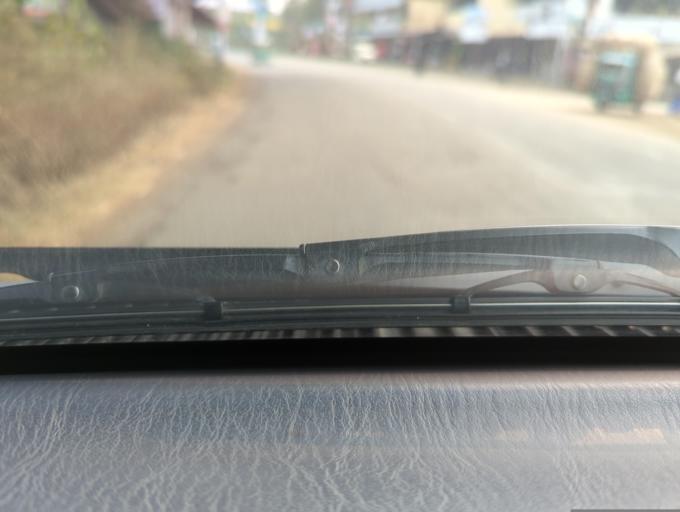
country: BD
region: Sylhet
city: Maulavi Bazar
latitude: 24.4986
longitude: 91.7358
